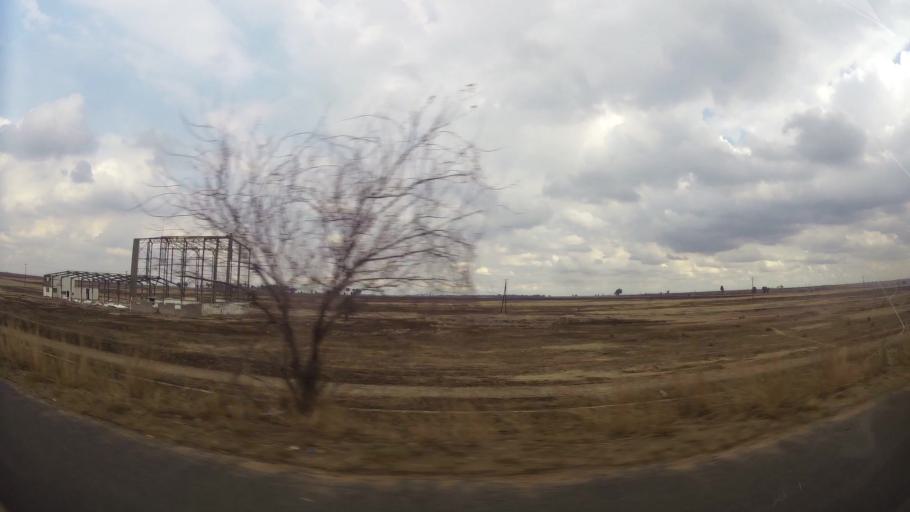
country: ZA
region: Orange Free State
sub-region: Fezile Dabi District Municipality
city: Sasolburg
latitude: -26.8662
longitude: 27.8922
